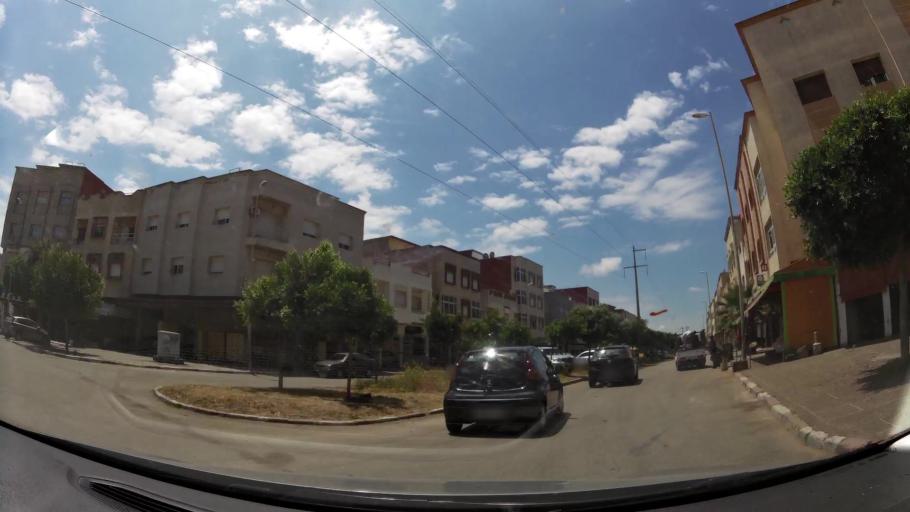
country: MA
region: Gharb-Chrarda-Beni Hssen
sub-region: Kenitra Province
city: Kenitra
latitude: 34.2680
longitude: -6.6157
